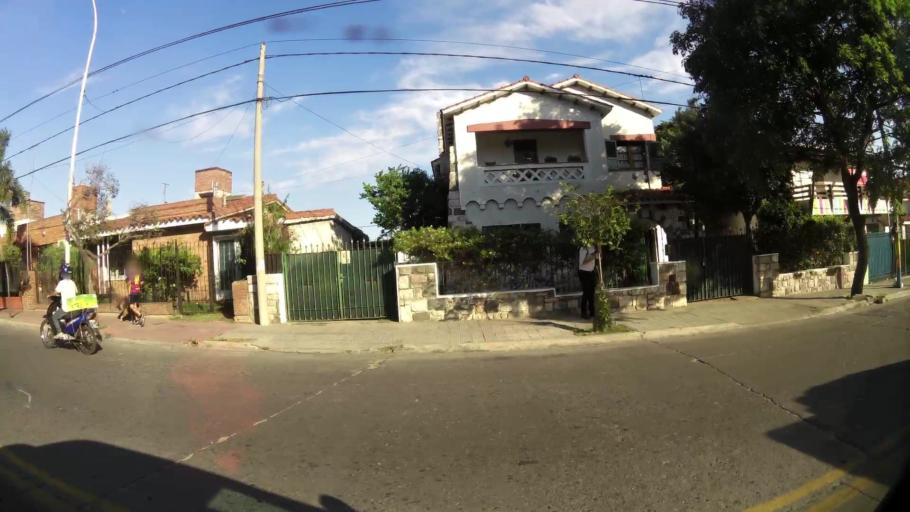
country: AR
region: Cordoba
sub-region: Departamento de Capital
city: Cordoba
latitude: -31.3837
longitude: -64.2242
